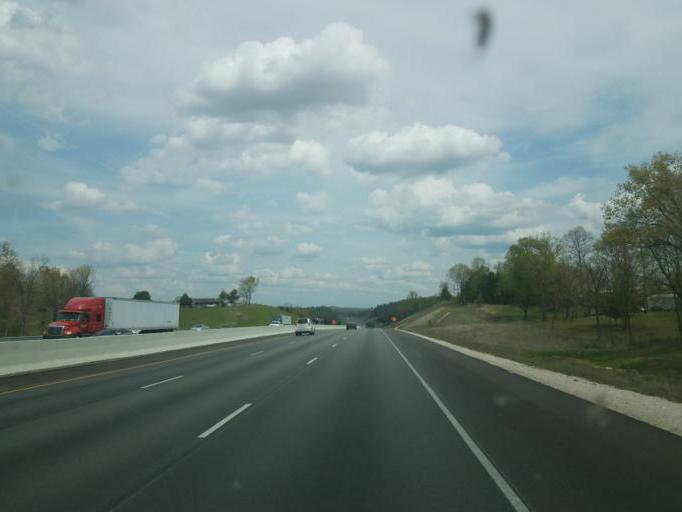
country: US
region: Kentucky
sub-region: Hart County
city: Munfordville
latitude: 37.3553
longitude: -85.8983
